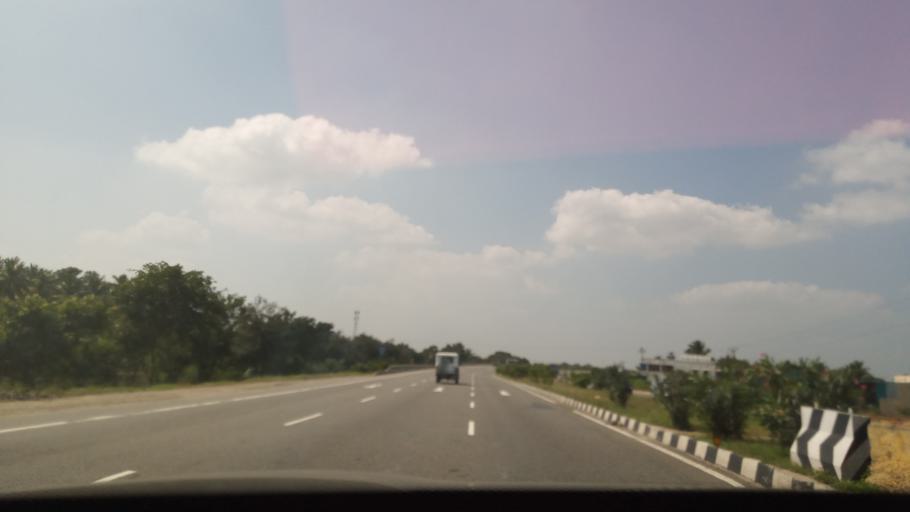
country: IN
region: Tamil Nadu
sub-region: Vellore
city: Walajapet
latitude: 12.9123
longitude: 79.3732
